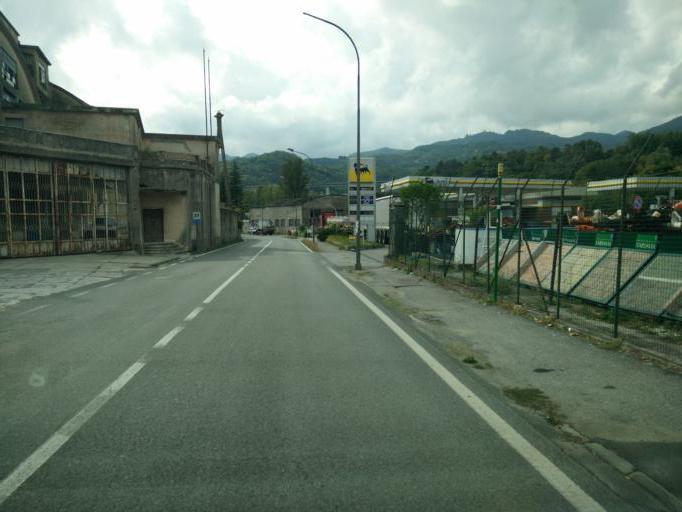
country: IT
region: Tuscany
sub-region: Provincia di Massa-Carrara
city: Pontremoli
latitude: 44.3689
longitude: 9.8857
